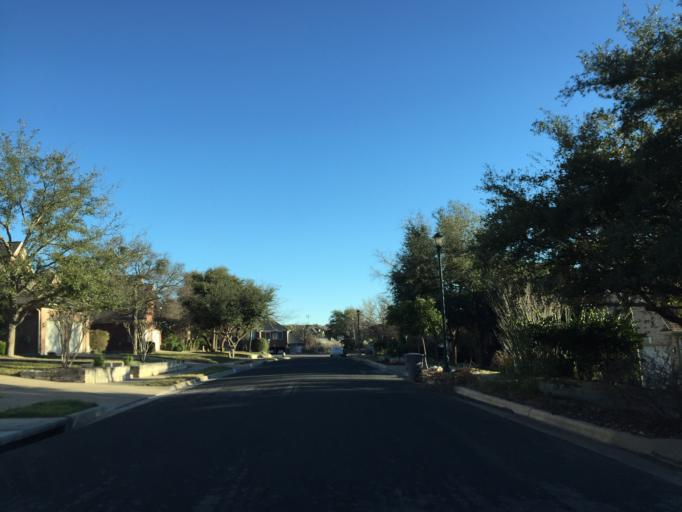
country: US
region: Texas
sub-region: Williamson County
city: Jollyville
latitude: 30.4307
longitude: -97.7872
